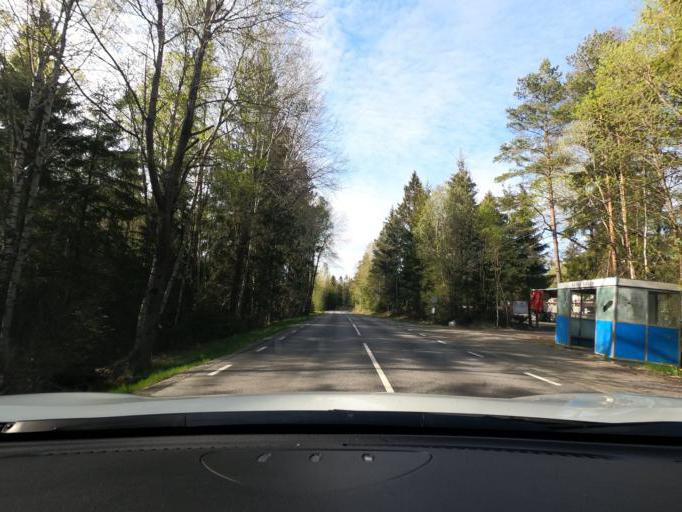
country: SE
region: Vaestra Goetaland
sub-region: Harryda Kommun
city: Landvetter
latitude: 57.6619
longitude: 12.2492
